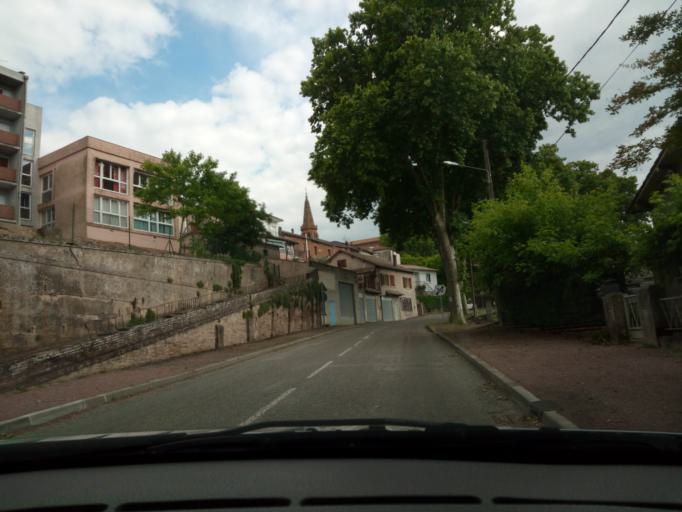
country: FR
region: Midi-Pyrenees
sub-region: Departement du Tarn-et-Garonne
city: Lafrancaise
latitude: 44.1270
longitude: 1.2394
